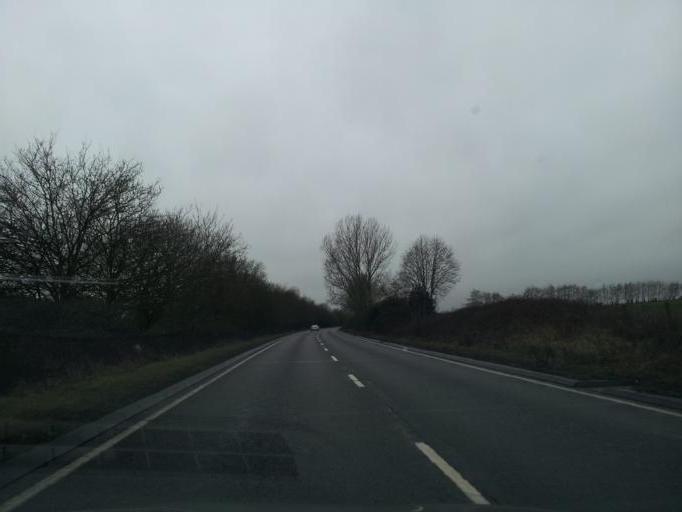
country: GB
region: England
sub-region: Essex
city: Mistley
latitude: 51.9097
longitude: 1.1269
